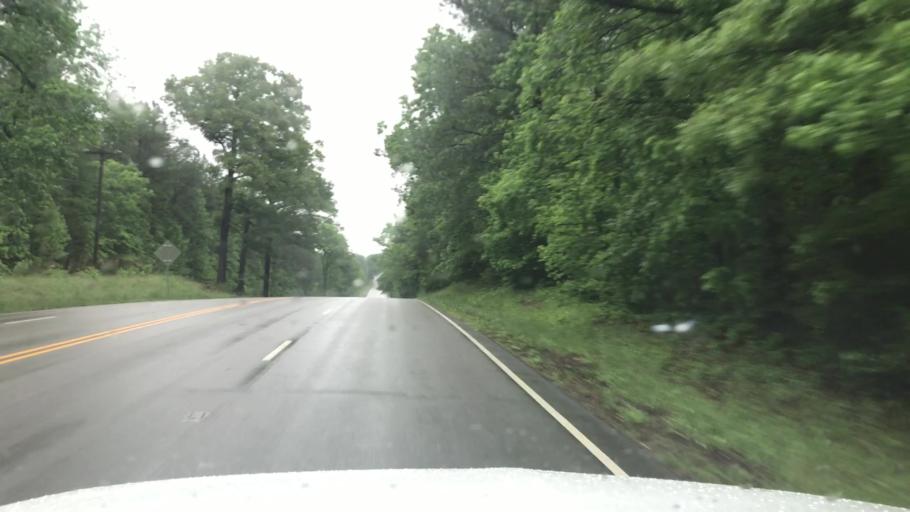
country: US
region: Virginia
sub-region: Hanover County
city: Ashland
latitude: 37.8342
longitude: -77.4686
